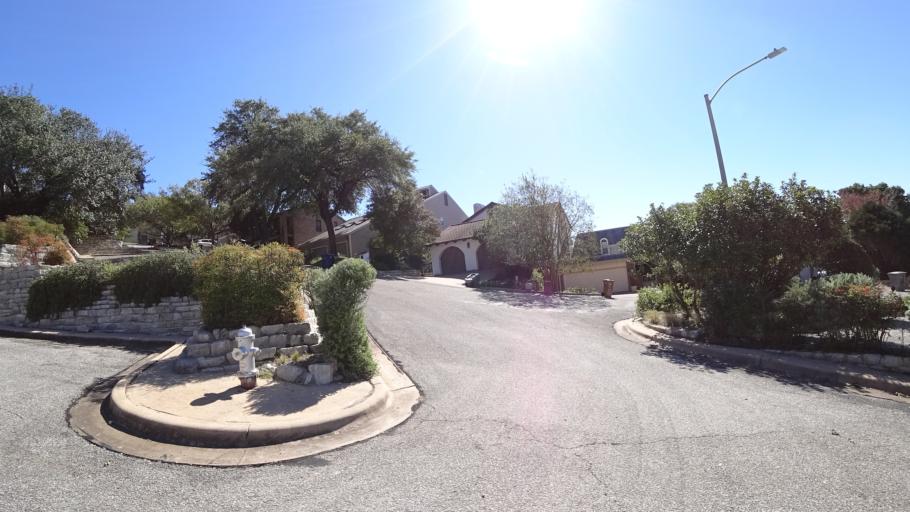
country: US
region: Texas
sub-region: Travis County
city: West Lake Hills
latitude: 30.3483
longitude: -97.7794
